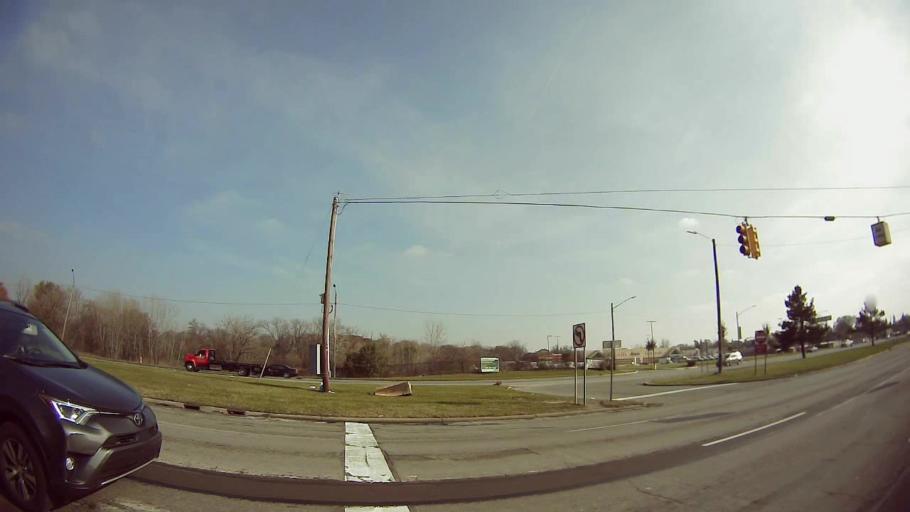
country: US
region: Michigan
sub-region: Wayne County
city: Redford
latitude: 42.4384
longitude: -83.2792
